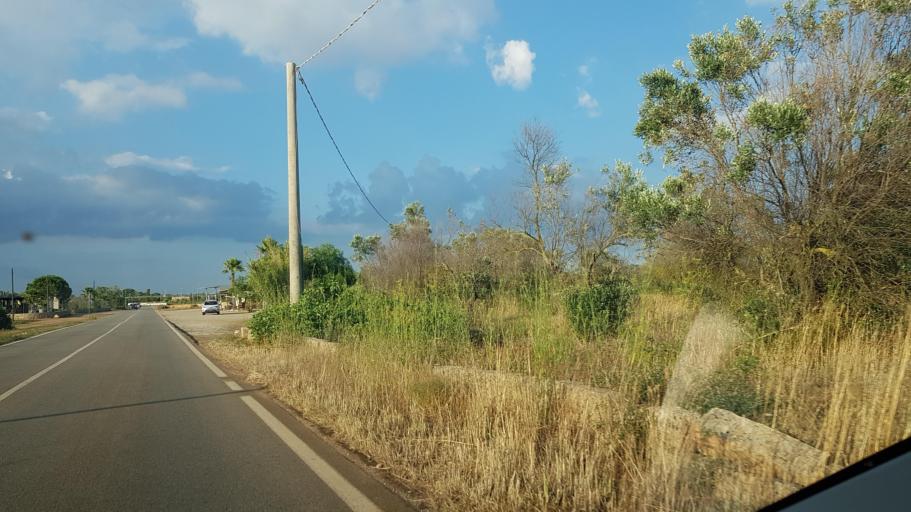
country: IT
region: Apulia
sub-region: Provincia di Lecce
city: Acquarica del Capo
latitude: 39.8714
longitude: 18.2218
